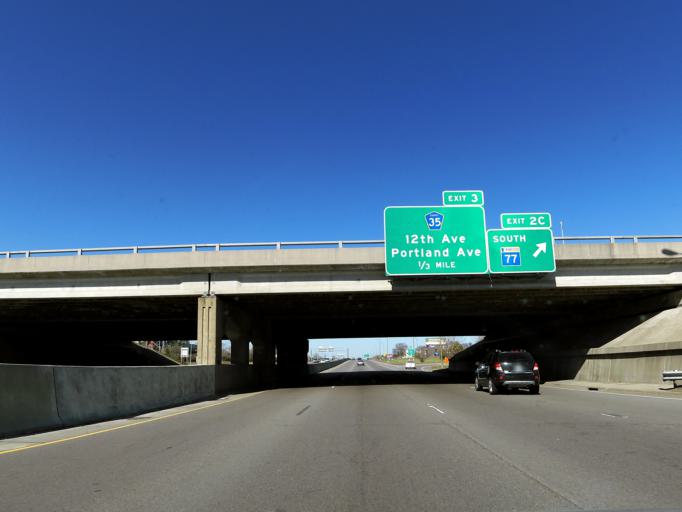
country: US
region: Minnesota
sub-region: Hennepin County
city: Richfield
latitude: 44.8623
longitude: -93.2468
